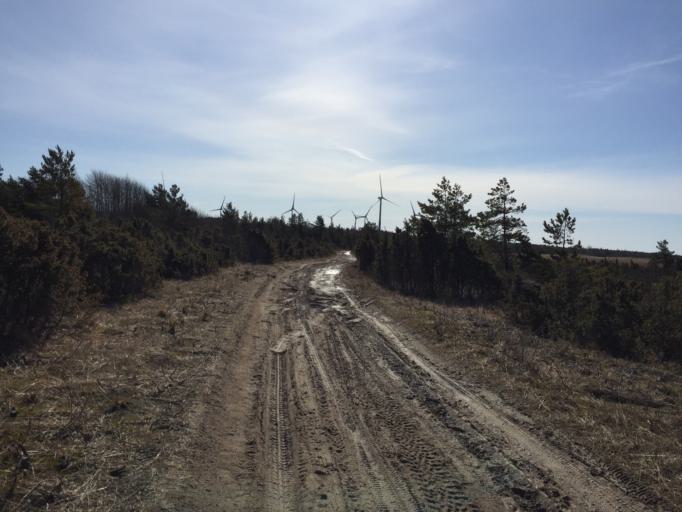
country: EE
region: Laeaene
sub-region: Haapsalu linn
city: Haapsalu
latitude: 58.6492
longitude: 23.5087
